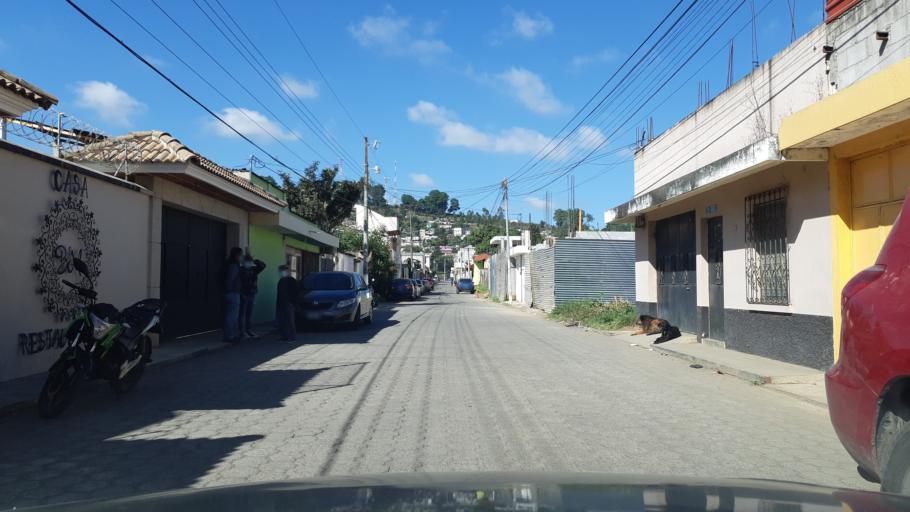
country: GT
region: Chimaltenango
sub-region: Municipio de Chimaltenango
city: Chimaltenango
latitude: 14.6515
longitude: -90.8155
